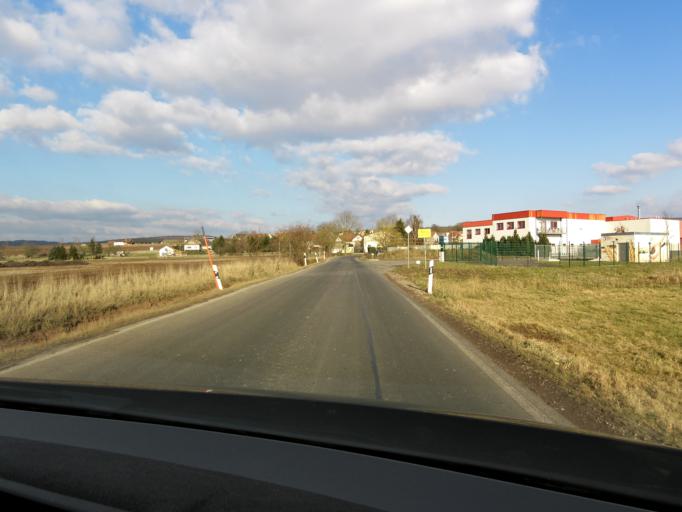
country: DE
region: Thuringia
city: Bad Salzungen
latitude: 50.8600
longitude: 10.2440
